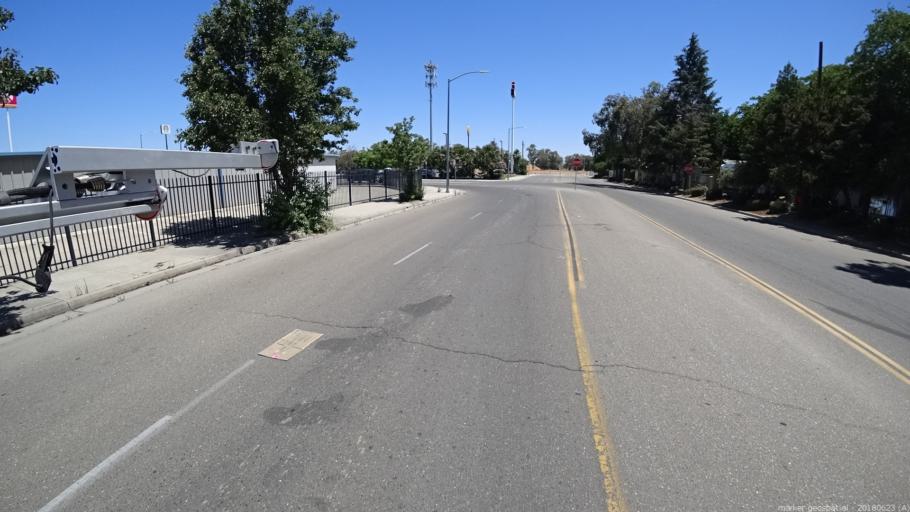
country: US
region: California
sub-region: Madera County
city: Chowchilla
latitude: 37.1243
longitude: -120.2556
